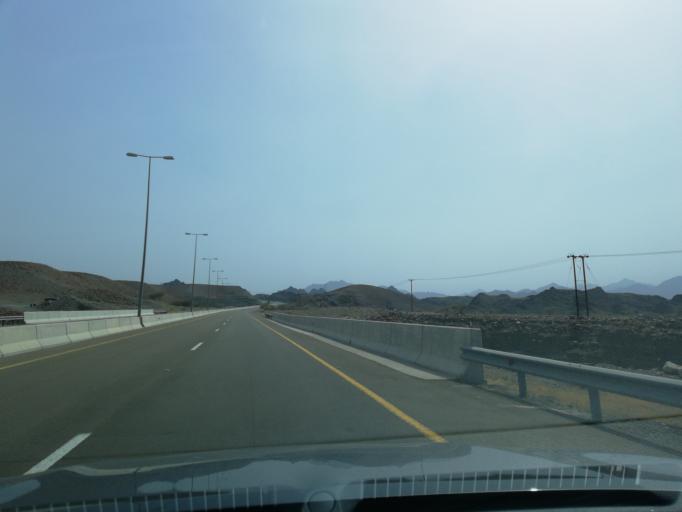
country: OM
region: Al Batinah
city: Al Liwa'
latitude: 24.2807
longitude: 56.4042
